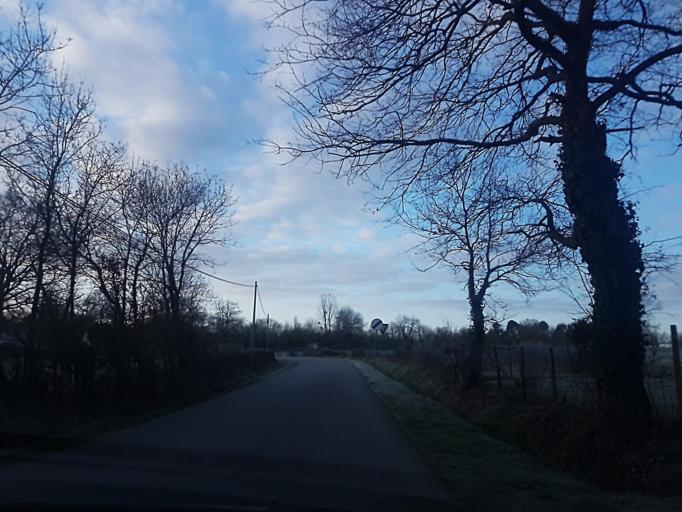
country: FR
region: Pays de la Loire
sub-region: Departement de la Loire-Atlantique
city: Petit-Mars
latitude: 47.3849
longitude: -1.4280
